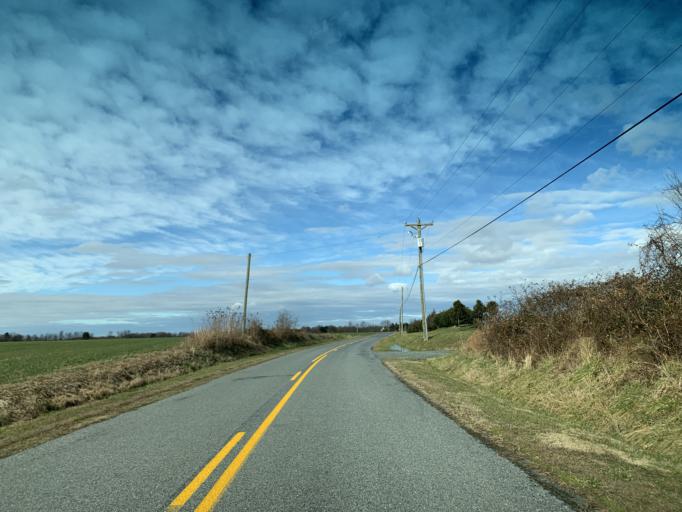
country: US
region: Maryland
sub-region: Kent County
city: Chestertown
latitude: 39.3438
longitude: -76.0524
